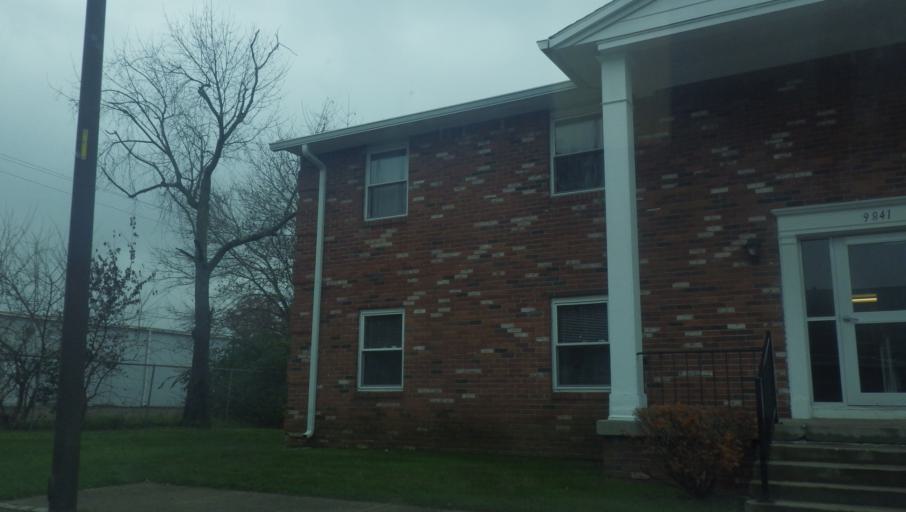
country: US
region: Indiana
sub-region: Marion County
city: Cumberland
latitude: 39.7979
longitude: -85.9927
